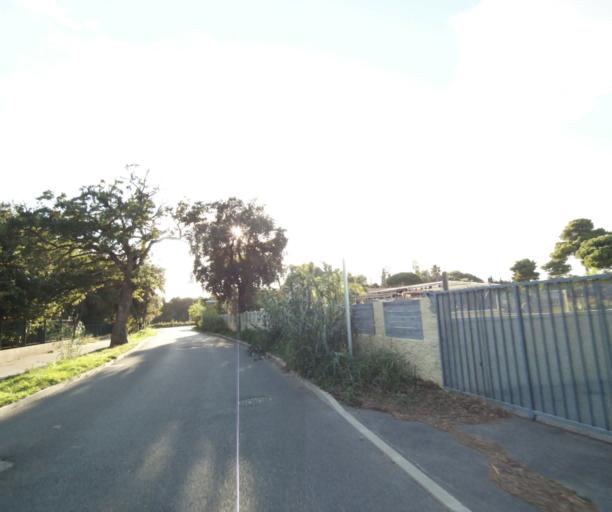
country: FR
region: Languedoc-Roussillon
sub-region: Departement des Pyrenees-Orientales
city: Argelers
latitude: 42.5729
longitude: 3.0157
